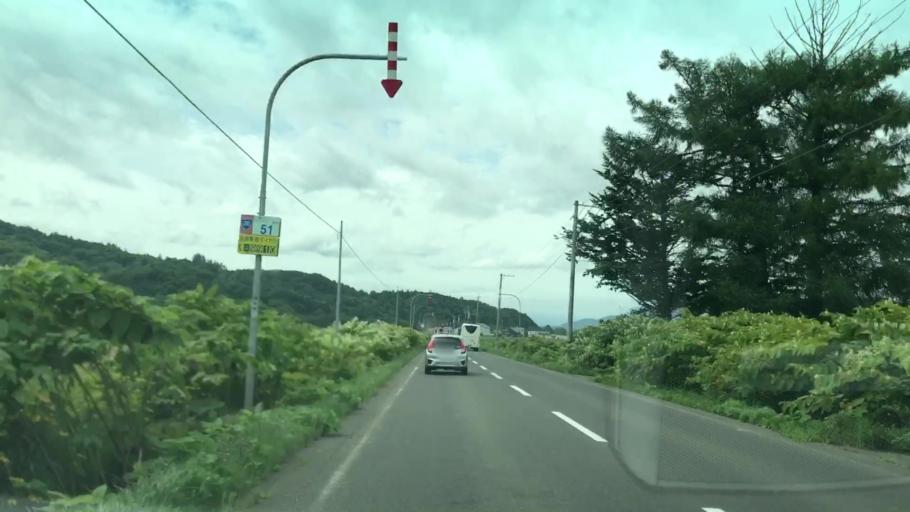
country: JP
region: Hokkaido
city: Niseko Town
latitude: 42.9427
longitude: 140.8192
